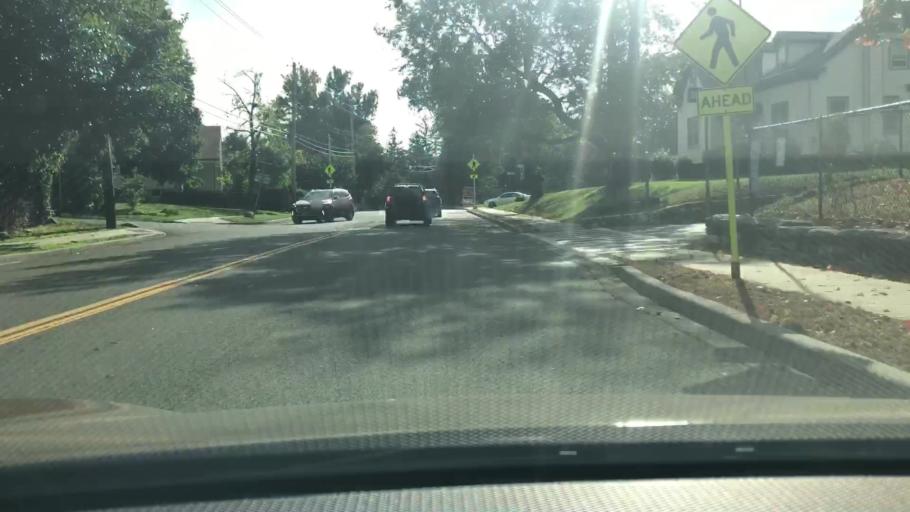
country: US
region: New York
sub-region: Westchester County
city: Tuckahoe
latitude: 40.9477
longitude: -73.8194
